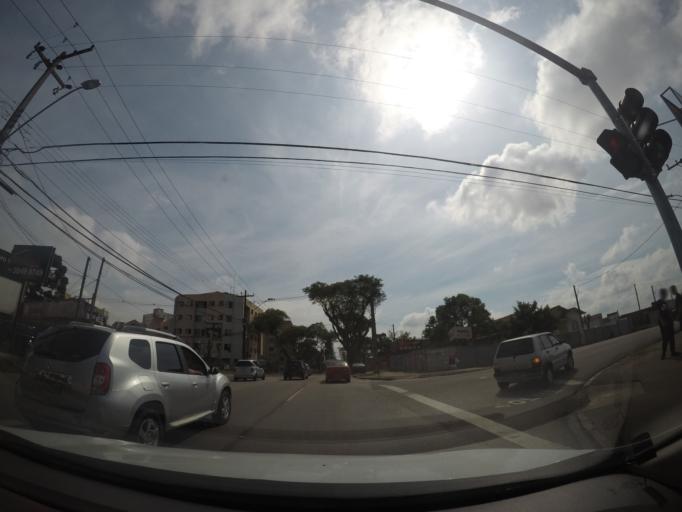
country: BR
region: Parana
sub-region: Curitiba
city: Curitiba
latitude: -25.4925
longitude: -49.2896
